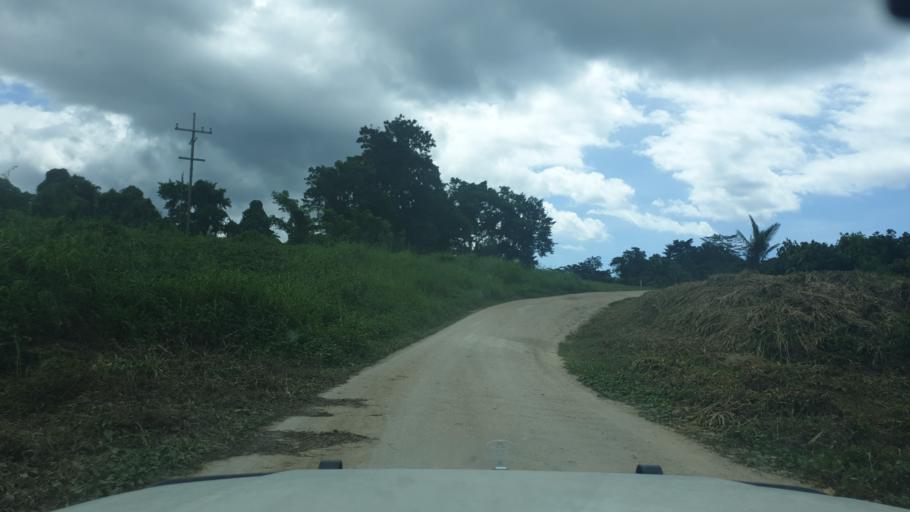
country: PG
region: Bougainville
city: Buka
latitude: -5.5403
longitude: 154.8296
